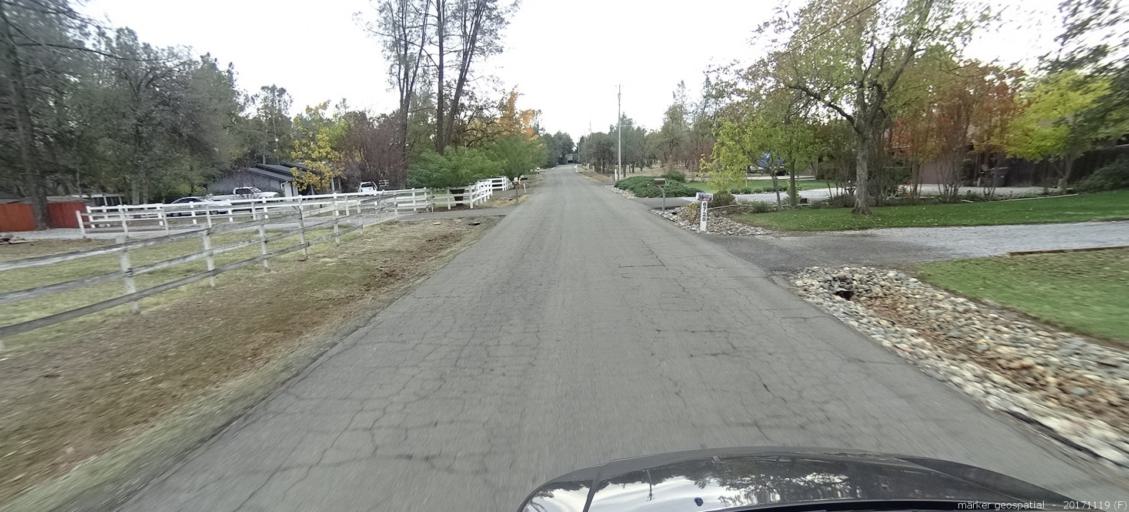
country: US
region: California
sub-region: Shasta County
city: Shasta
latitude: 40.4804
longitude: -122.4641
